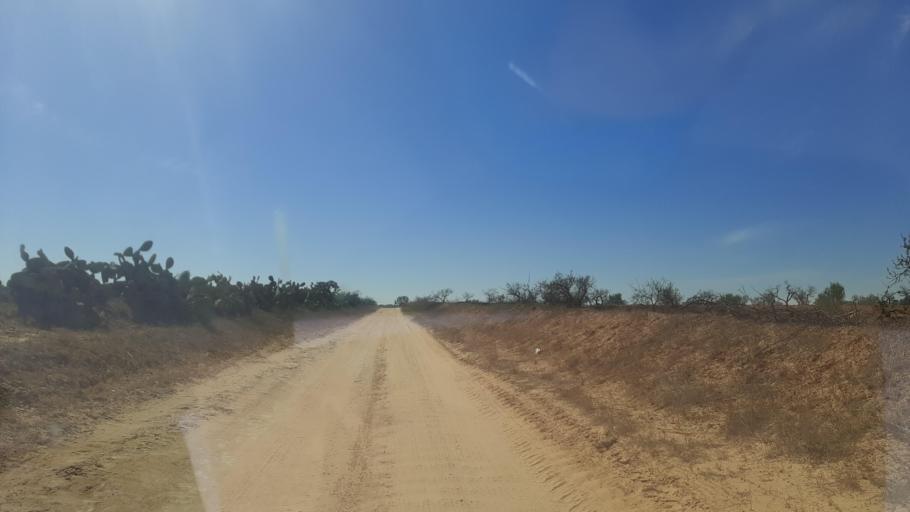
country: TN
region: Safaqis
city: Sfax
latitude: 34.8372
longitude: 10.5584
